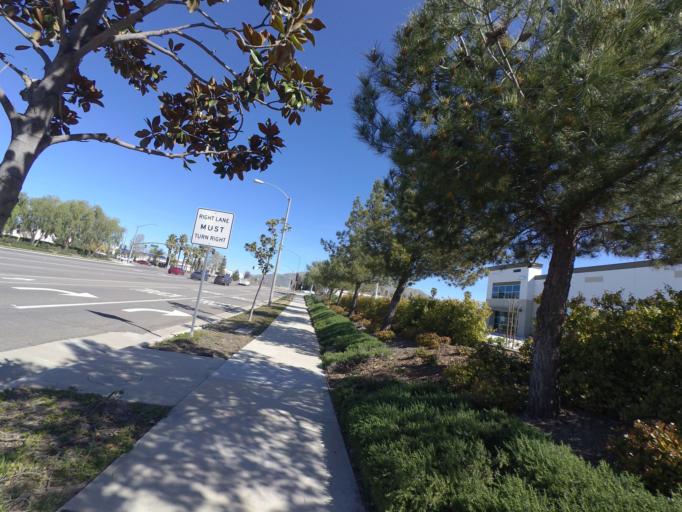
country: US
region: California
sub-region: Riverside County
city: March Air Force Base
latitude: 33.9157
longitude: -117.2917
